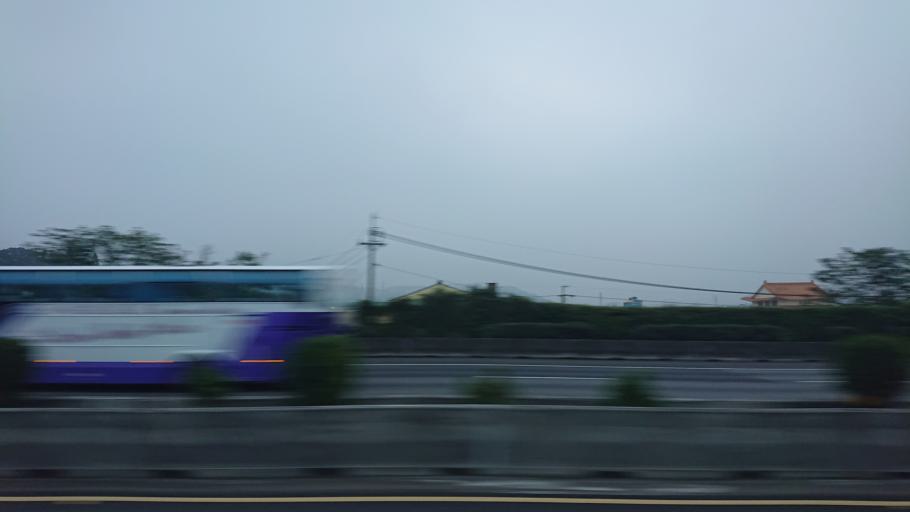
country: TW
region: Taiwan
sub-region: Hsinchu
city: Hsinchu
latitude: 24.7016
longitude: 120.9260
